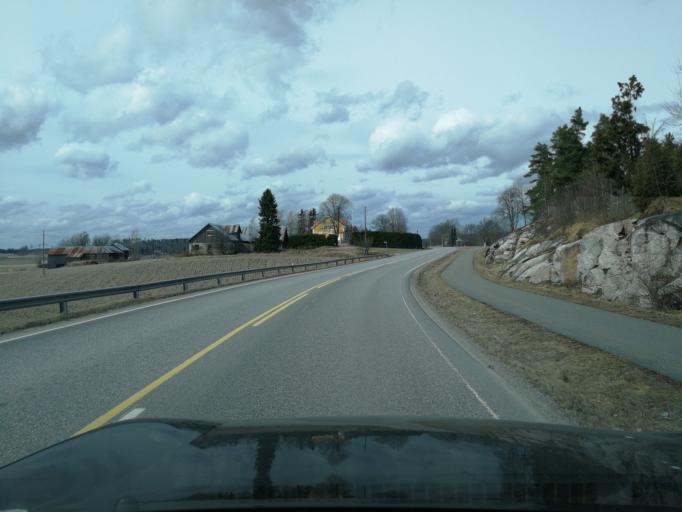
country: FI
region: Uusimaa
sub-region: Helsinki
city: Siuntio
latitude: 60.1528
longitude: 24.2072
